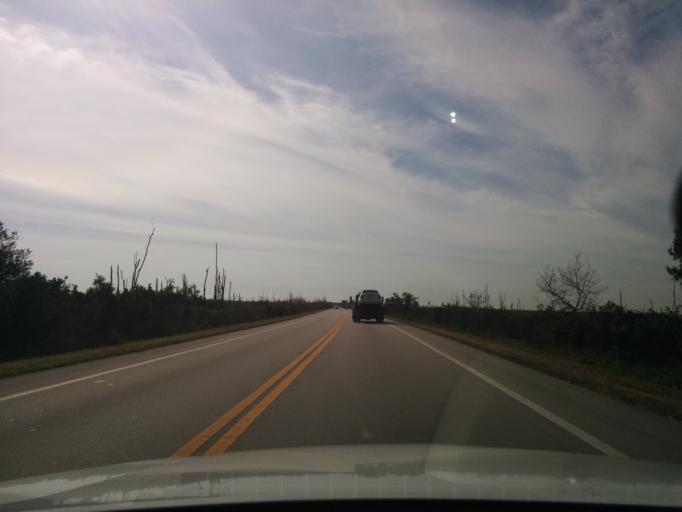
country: US
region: Florida
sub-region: Miami-Dade County
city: Tamiami
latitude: 25.7976
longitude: -80.4828
